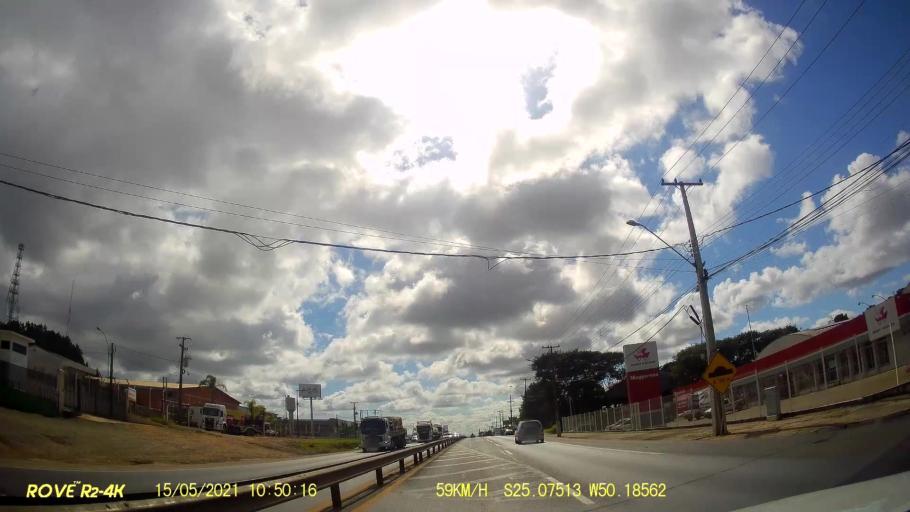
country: BR
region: Parana
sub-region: Ponta Grossa
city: Ponta Grossa
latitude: -25.0751
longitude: -50.1856
